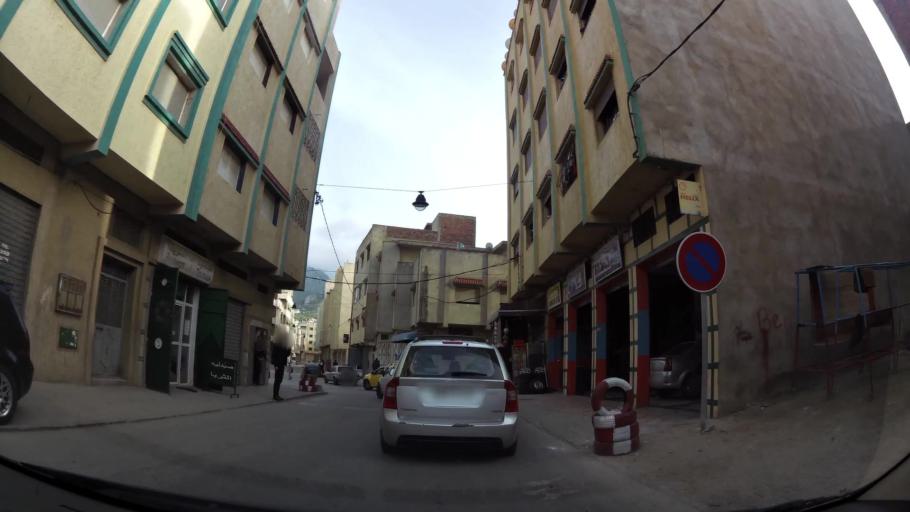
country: MA
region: Tanger-Tetouan
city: Tetouan
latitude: 35.5626
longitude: -5.3959
